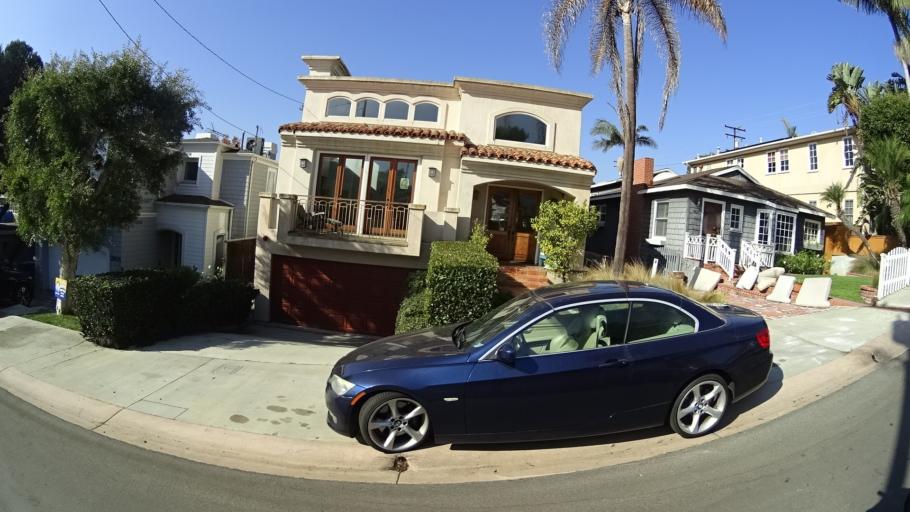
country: US
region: California
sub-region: Los Angeles County
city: Manhattan Beach
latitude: 33.8954
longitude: -118.3987
